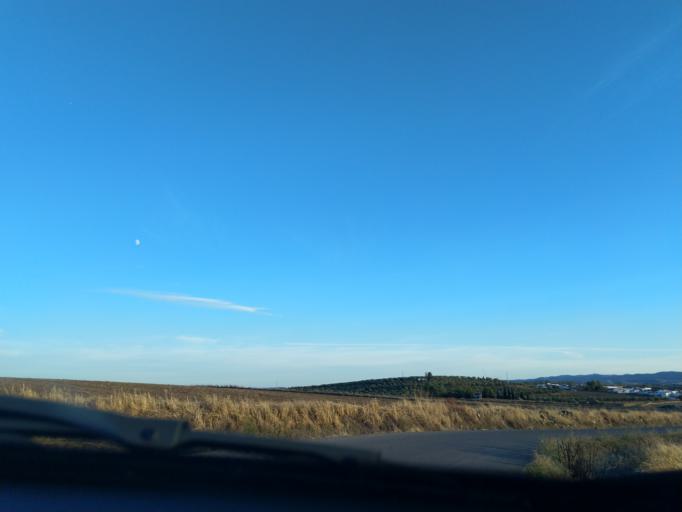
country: ES
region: Extremadura
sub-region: Provincia de Badajoz
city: Valverde de Llerena
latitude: 38.2224
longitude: -5.8223
